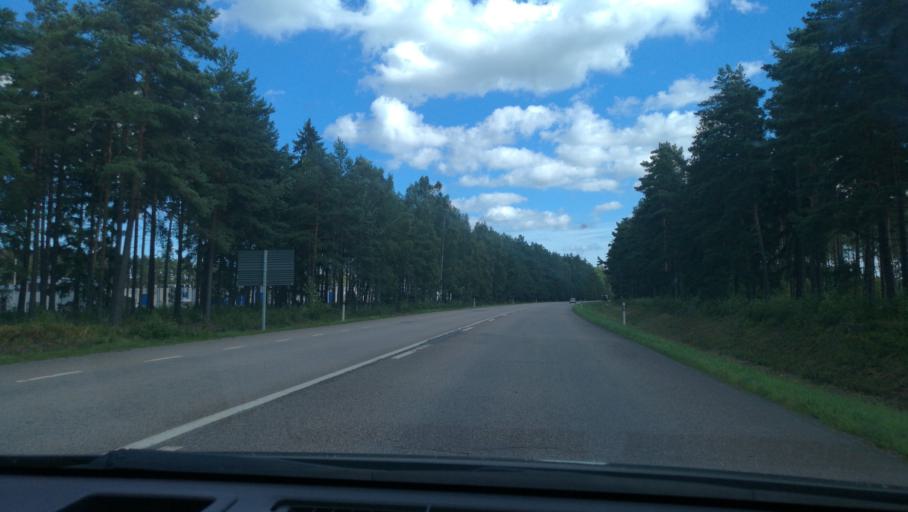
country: SE
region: Vaestra Goetaland
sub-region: Lidkopings Kommun
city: Lidkoping
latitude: 58.4918
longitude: 13.1943
